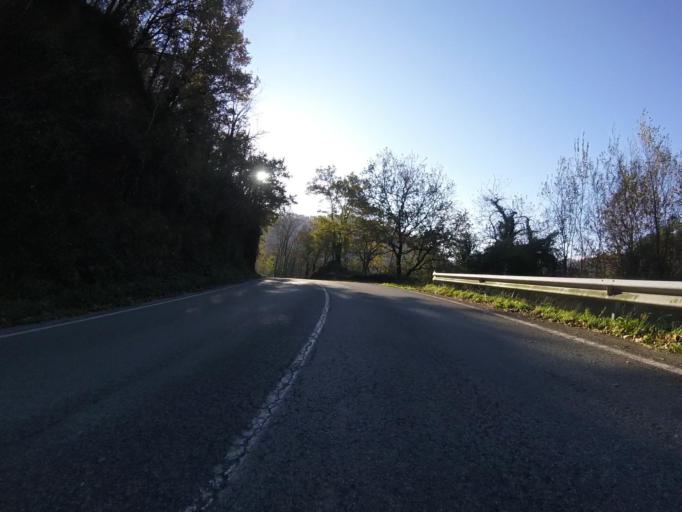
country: ES
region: Navarre
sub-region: Provincia de Navarra
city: Lesaka
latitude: 43.2410
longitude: -1.6732
